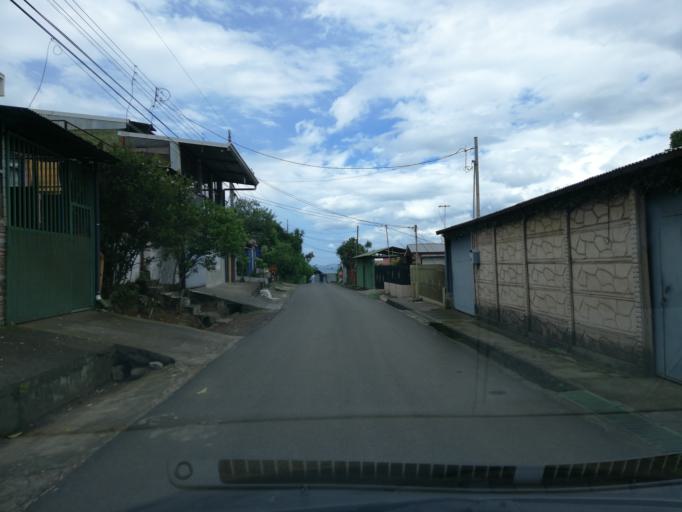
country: CR
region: Alajuela
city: Alajuela
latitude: 9.9990
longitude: -84.2107
